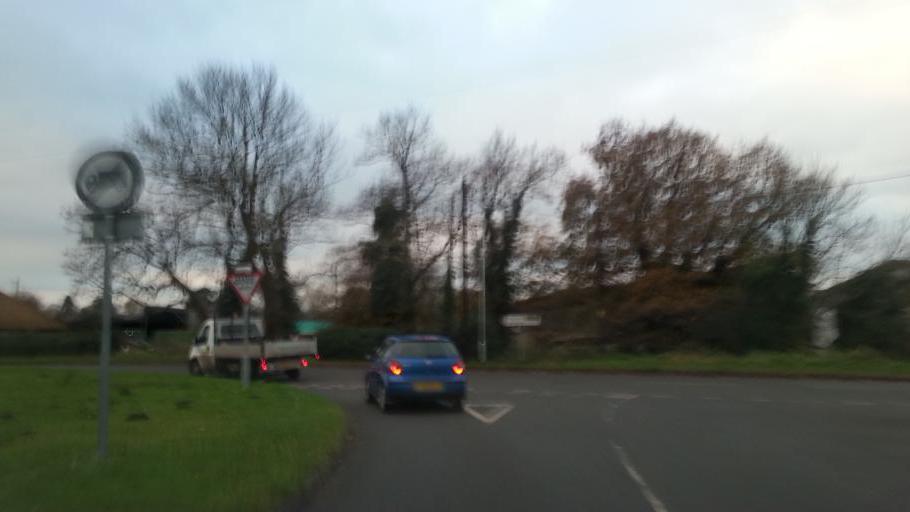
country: GB
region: England
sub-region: Nottinghamshire
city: Newark on Trent
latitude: 53.0951
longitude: -0.8462
